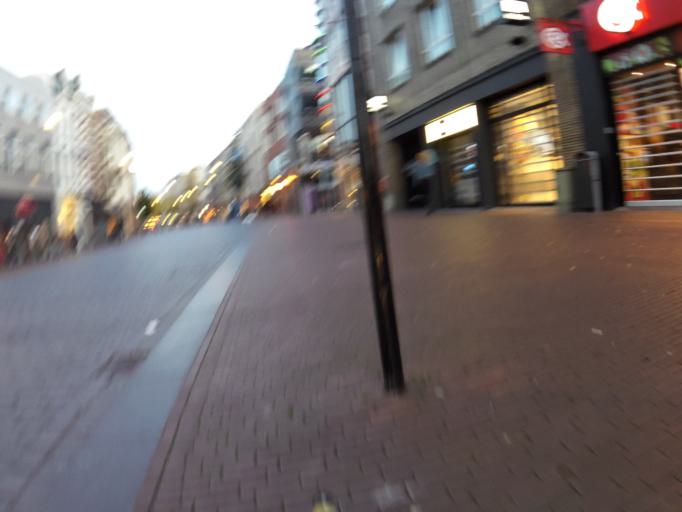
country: NL
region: Gelderland
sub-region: Gemeente Nijmegen
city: Nijmegen
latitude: 51.8467
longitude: 5.8665
